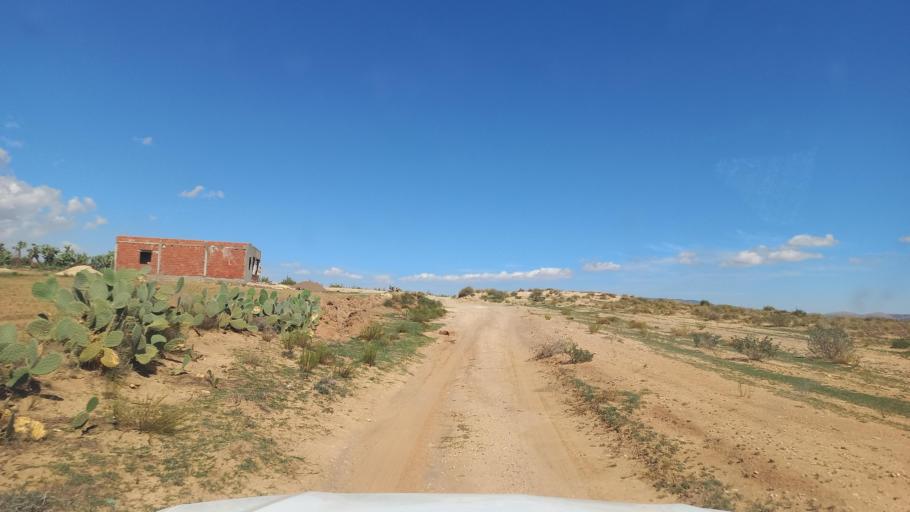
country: TN
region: Al Qasrayn
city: Sbiba
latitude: 35.3498
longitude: 9.0169
